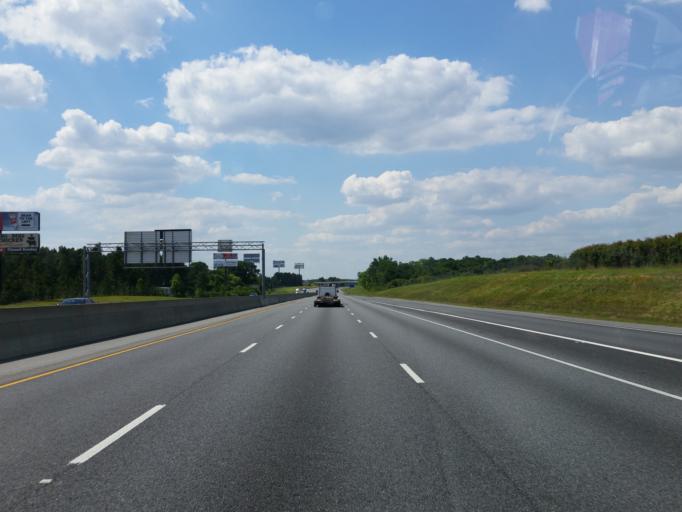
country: US
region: Georgia
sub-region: Turner County
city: Ashburn
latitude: 31.6830
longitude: -83.6216
